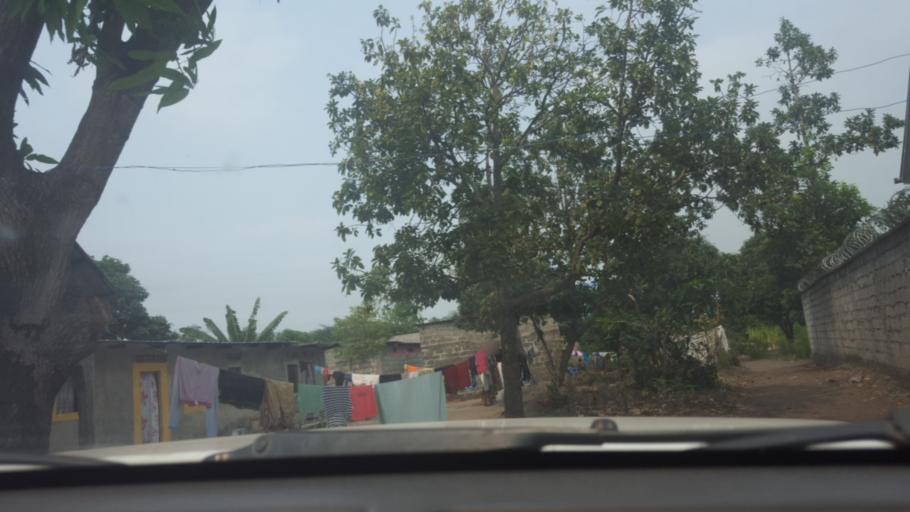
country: CD
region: Kinshasa
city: Masina
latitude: -4.3594
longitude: 15.5125
